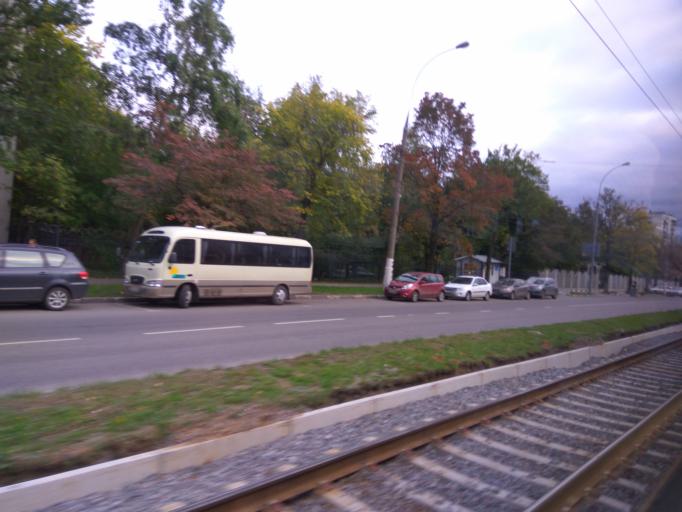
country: RU
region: Moscow
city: Chertanovo Yuzhnoye
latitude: 55.6191
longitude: 37.5937
